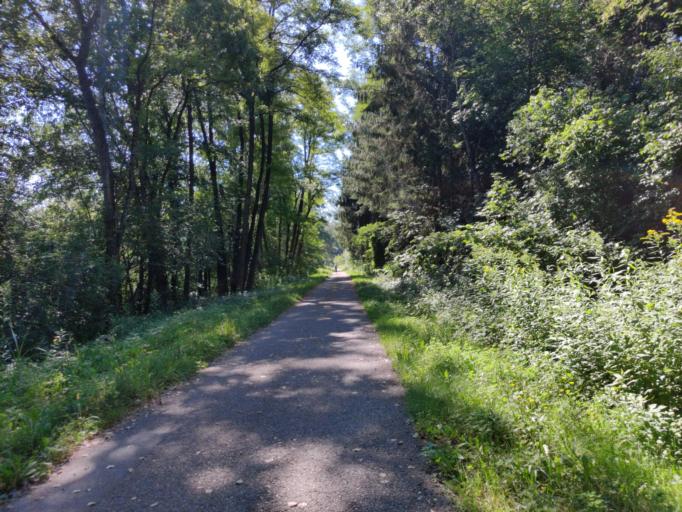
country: AT
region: Styria
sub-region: Politischer Bezirk Graz-Umgebung
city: Werndorf
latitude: 46.8998
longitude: 15.4948
